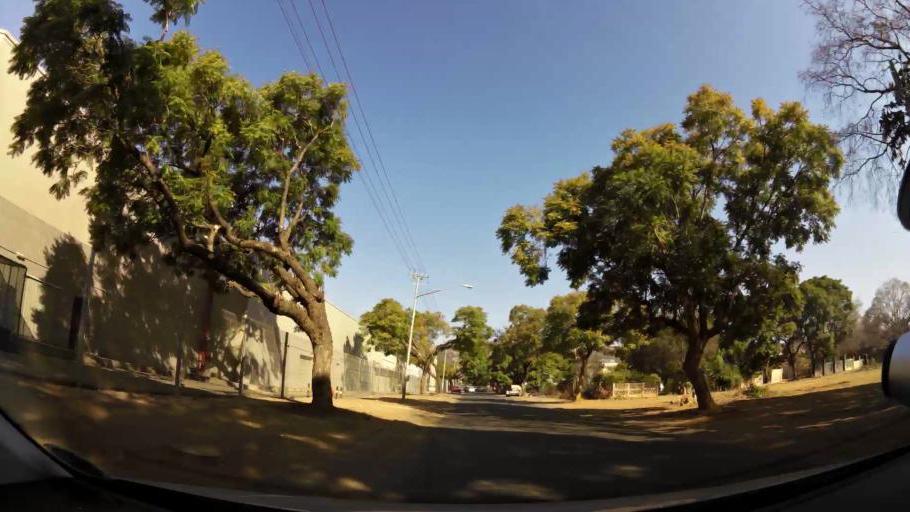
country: ZA
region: Gauteng
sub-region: City of Tshwane Metropolitan Municipality
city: Pretoria
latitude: -25.6732
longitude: 28.1727
